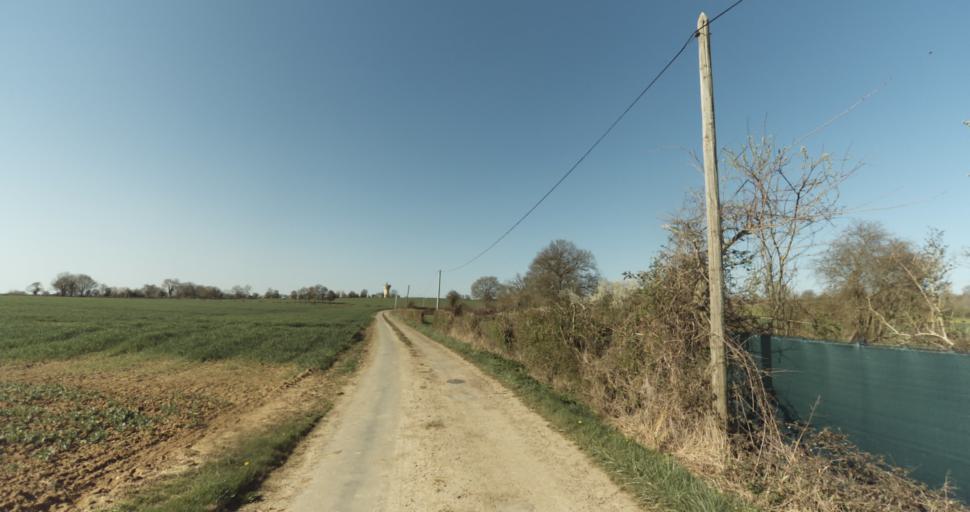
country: FR
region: Lower Normandy
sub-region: Departement du Calvados
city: Saint-Pierre-sur-Dives
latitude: 48.9341
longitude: -0.0056
